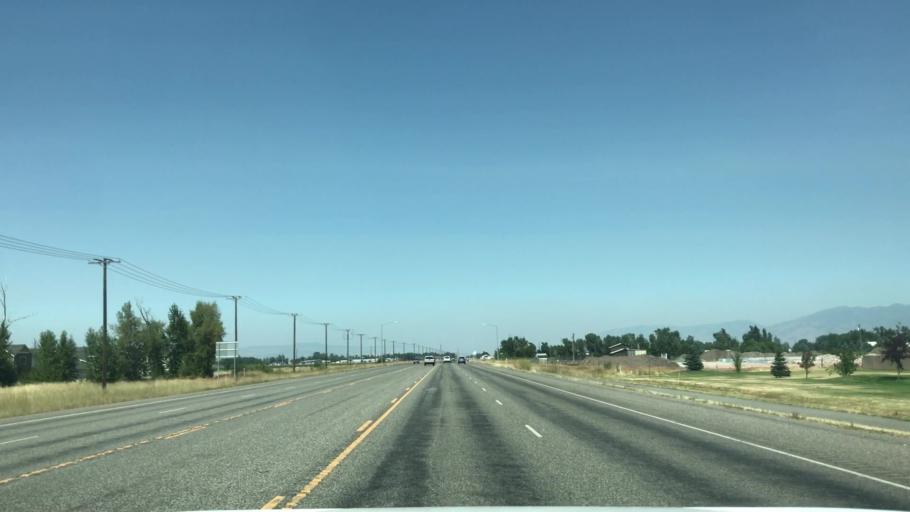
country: US
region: Montana
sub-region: Gallatin County
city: Four Corners
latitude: 45.6831
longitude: -111.1858
